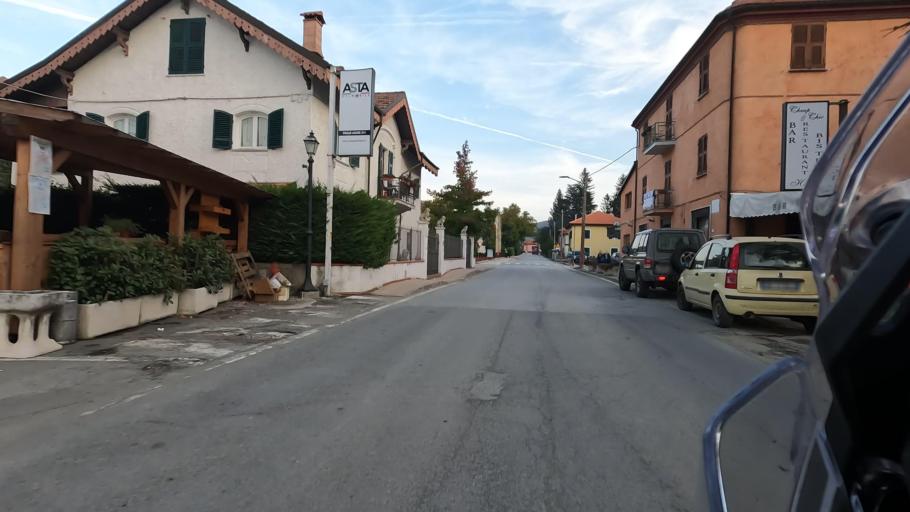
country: IT
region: Liguria
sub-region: Provincia di Savona
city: Pontinvrea
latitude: 44.4446
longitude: 8.4348
